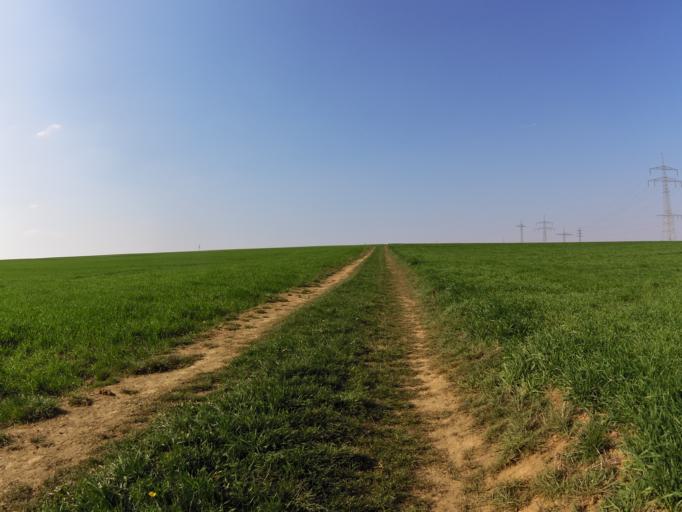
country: DE
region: Bavaria
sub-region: Regierungsbezirk Unterfranken
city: Theilheim
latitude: 49.7607
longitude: 10.0503
